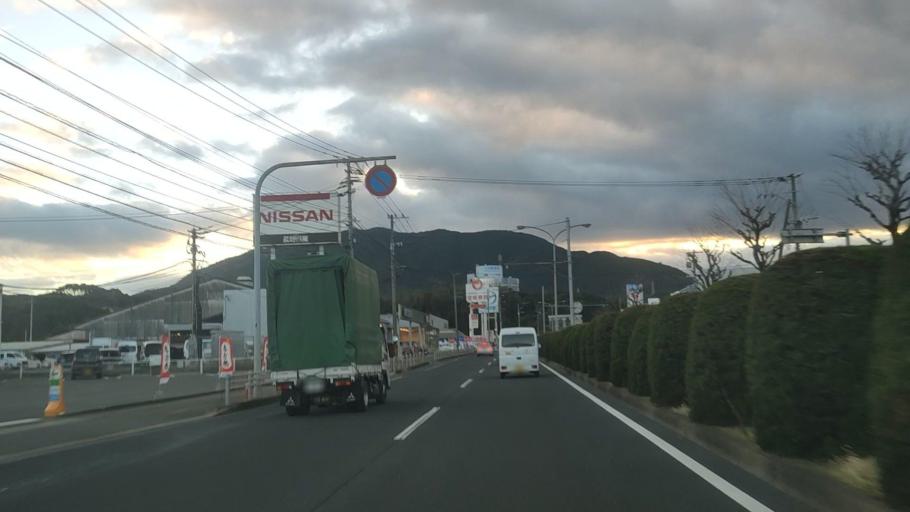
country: JP
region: Nagasaki
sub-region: Isahaya-shi
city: Isahaya
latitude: 32.8326
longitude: 130.0019
